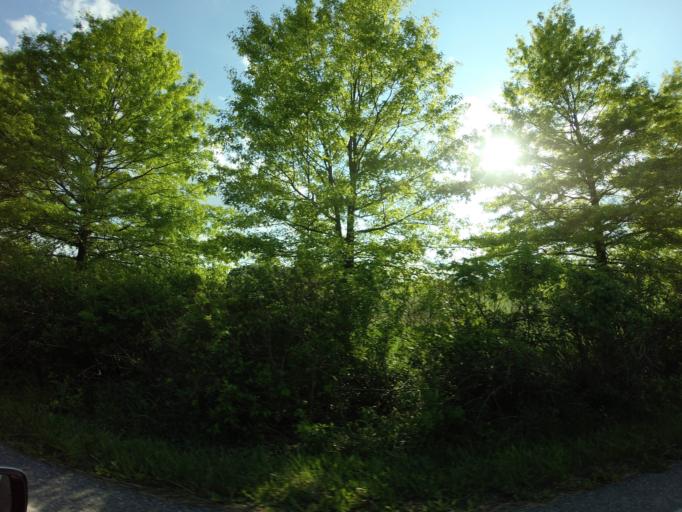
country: US
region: Maryland
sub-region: Baltimore County
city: Cockeysville
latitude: 39.4694
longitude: -76.7017
